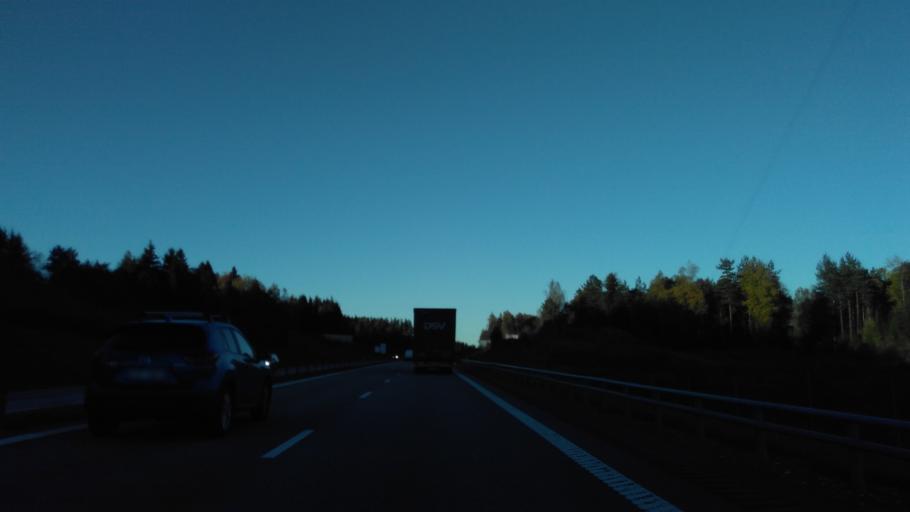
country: SE
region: Vaestra Goetaland
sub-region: Boras Kommun
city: Dalsjofors
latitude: 57.7684
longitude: 13.1129
